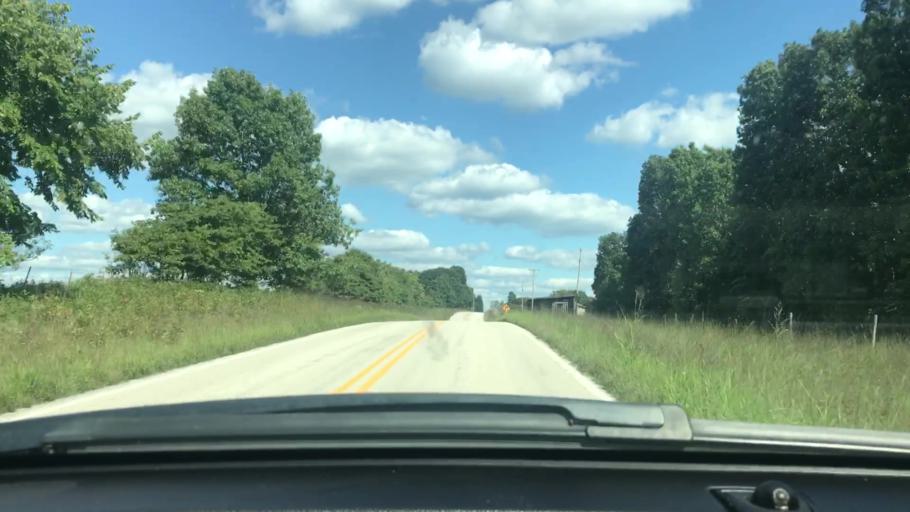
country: US
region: Missouri
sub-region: Wright County
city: Hartville
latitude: 37.3769
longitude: -92.4112
